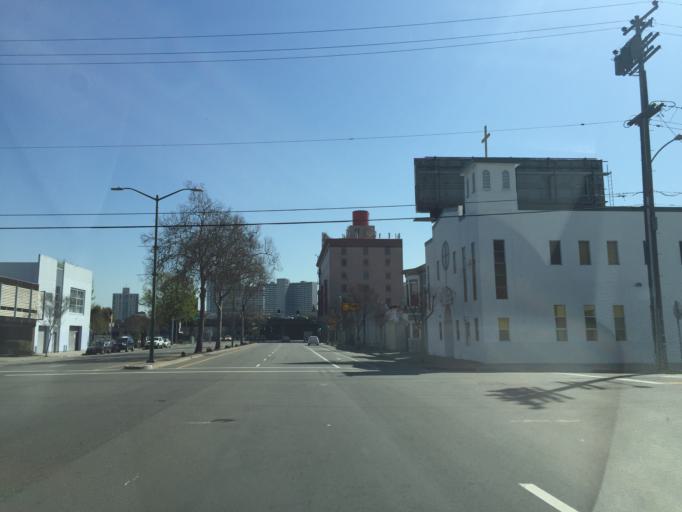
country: US
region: California
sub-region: Alameda County
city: Oakland
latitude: 37.8135
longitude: -122.2761
